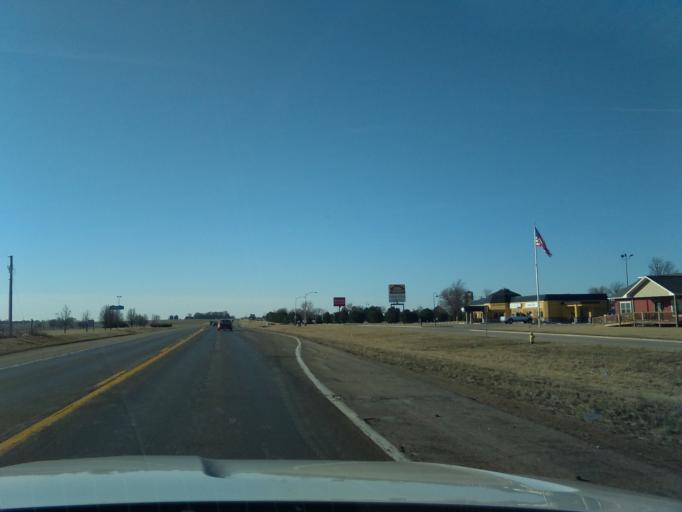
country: US
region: Nebraska
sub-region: Seward County
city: Seward
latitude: 40.8784
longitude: -97.1017
